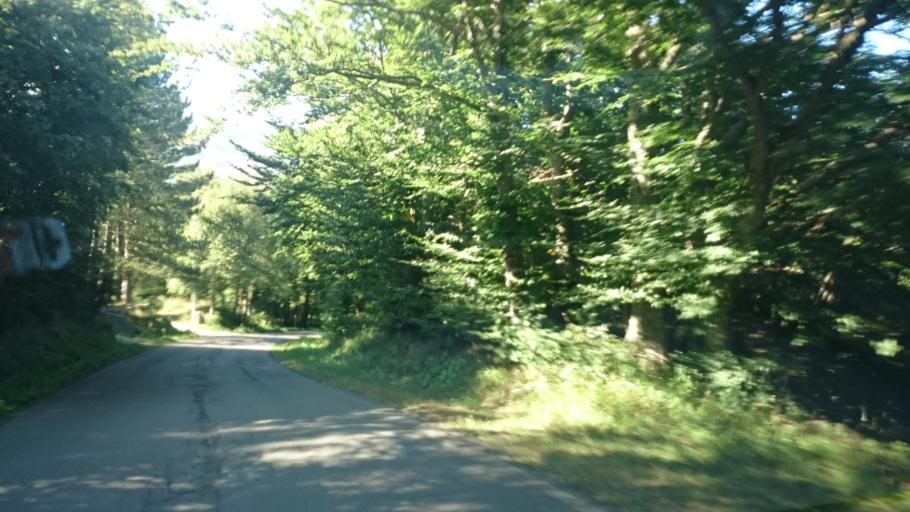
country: IT
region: Emilia-Romagna
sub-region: Provincia di Reggio Emilia
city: Villa Minozzo
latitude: 44.3031
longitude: 10.4281
